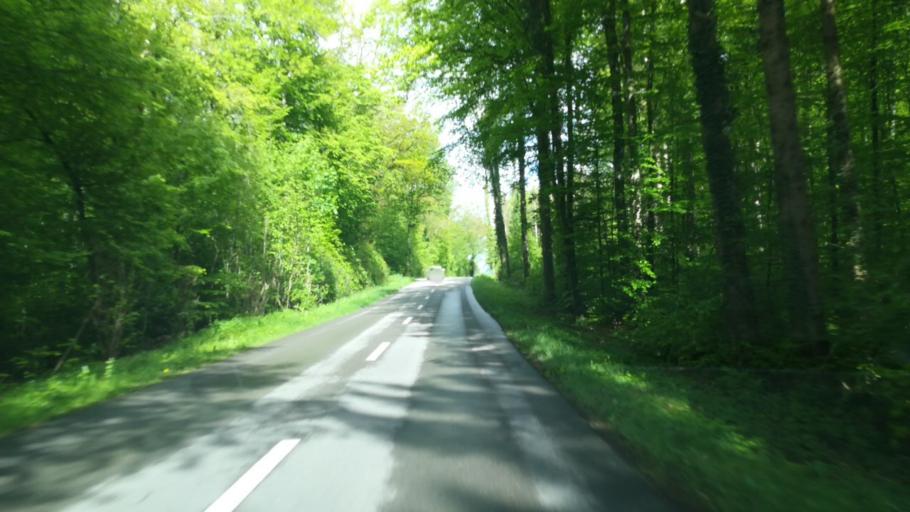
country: DE
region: Baden-Wuerttemberg
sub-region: Freiburg Region
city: Gailingen
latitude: 47.7158
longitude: 8.7305
